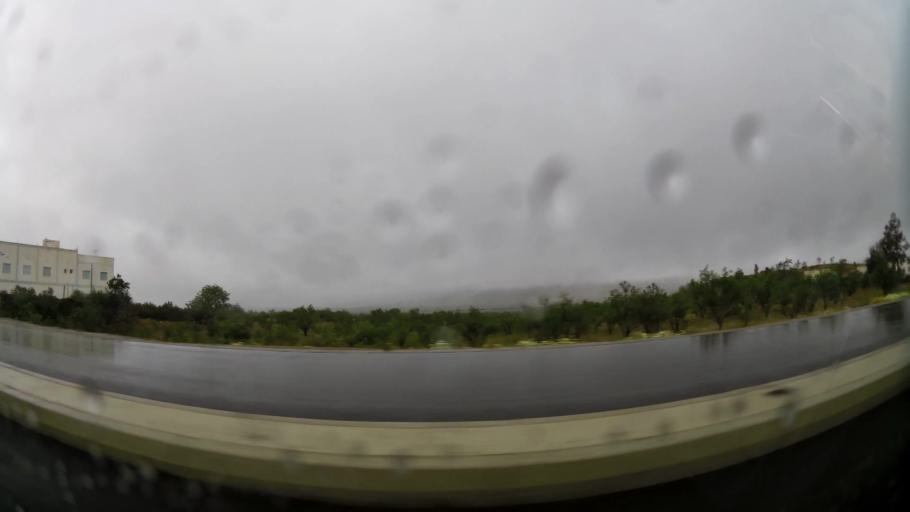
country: MA
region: Oriental
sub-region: Nador
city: Midar
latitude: 34.8579
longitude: -3.7222
